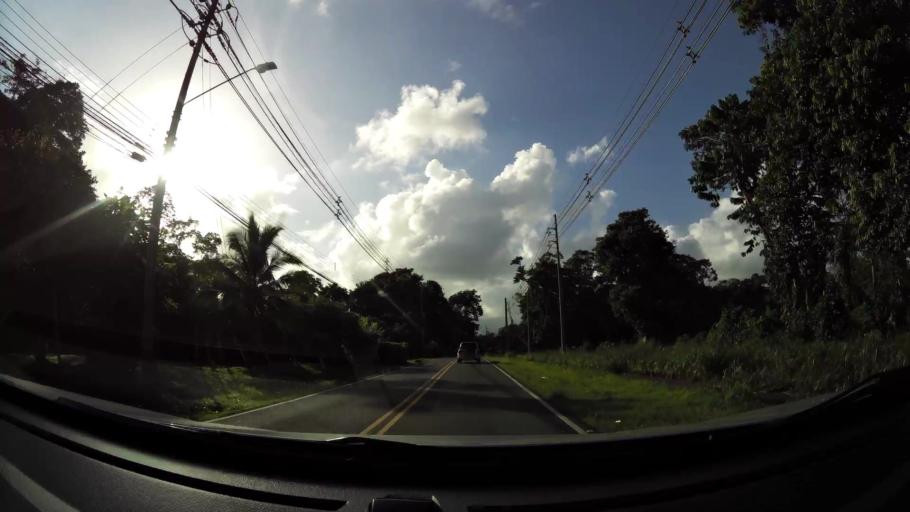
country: CR
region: Limon
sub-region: Canton de Siquirres
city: Siquirres
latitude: 10.0965
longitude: -83.5223
